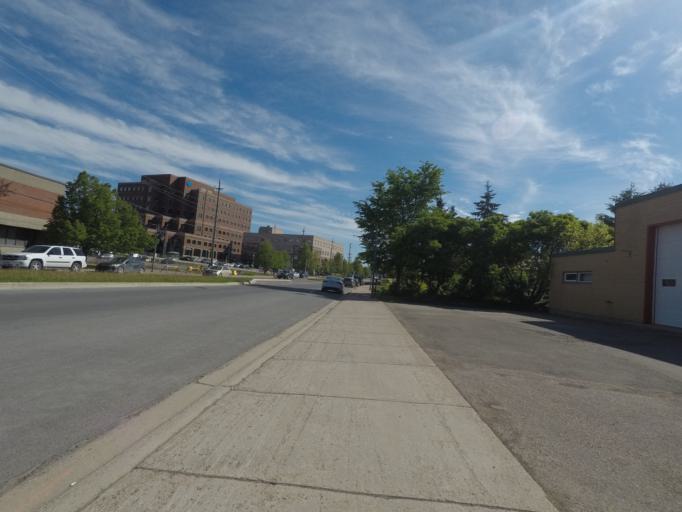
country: CA
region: New Brunswick
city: Moncton
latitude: 46.0868
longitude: -64.7749
